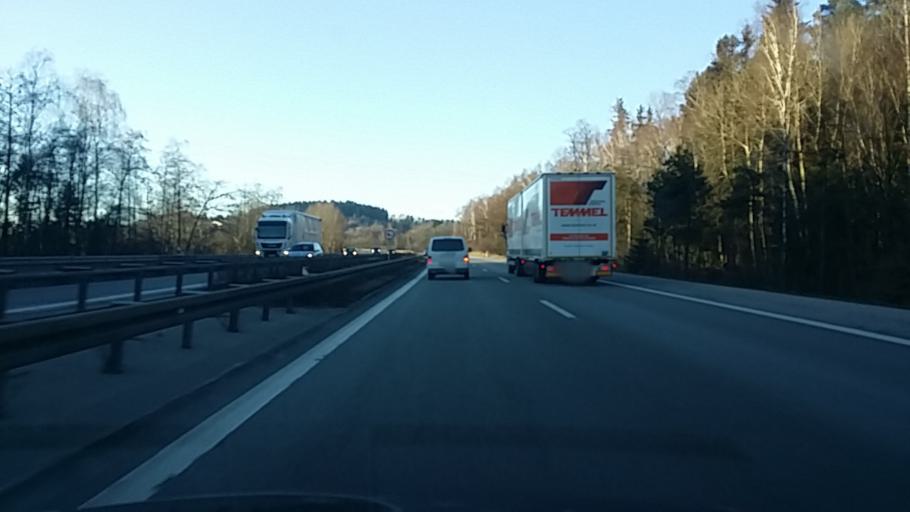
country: DE
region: Bavaria
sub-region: Lower Bavaria
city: Aicha vorm Wald
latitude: 48.6315
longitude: 13.3191
